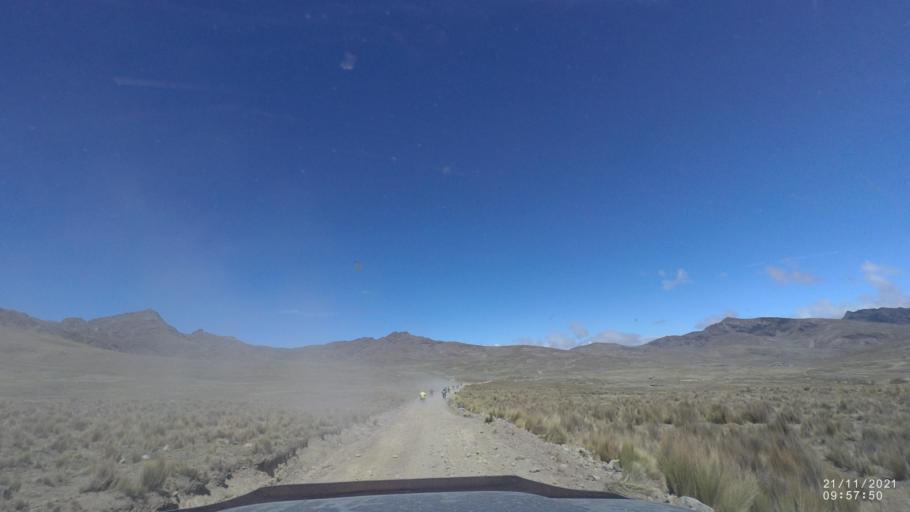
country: BO
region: Cochabamba
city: Cochabamba
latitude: -17.0380
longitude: -66.2734
